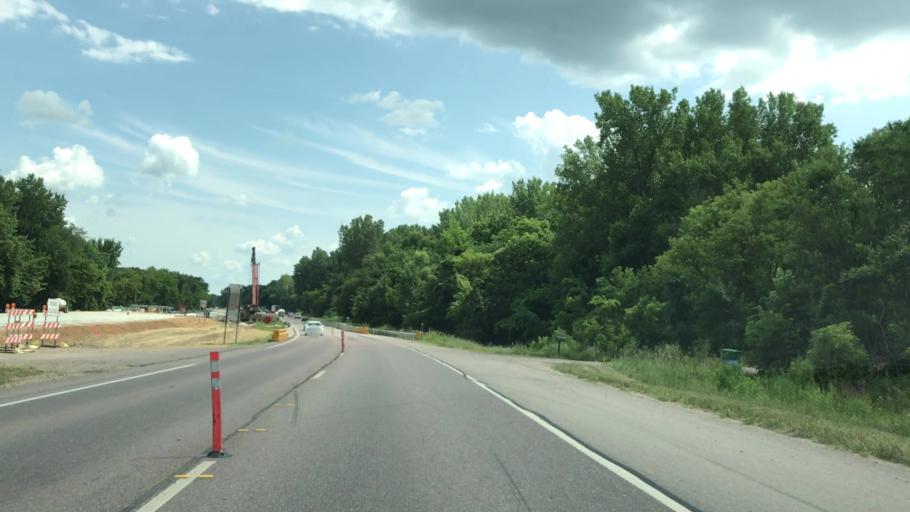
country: US
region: Minnesota
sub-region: Nicollet County
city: Saint Peter
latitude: 44.3670
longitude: -93.9646
